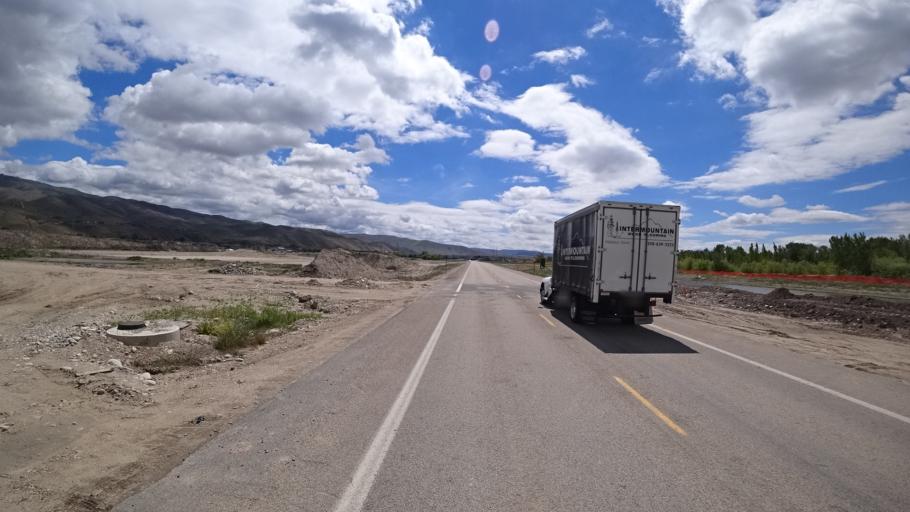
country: US
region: Idaho
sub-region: Ada County
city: Boise
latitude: 43.5726
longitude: -116.1376
